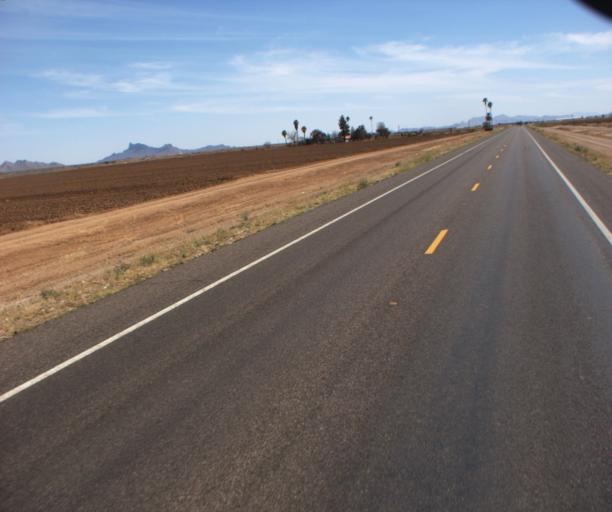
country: US
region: Arizona
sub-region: Pinal County
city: Eloy
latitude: 32.7735
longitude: -111.5155
